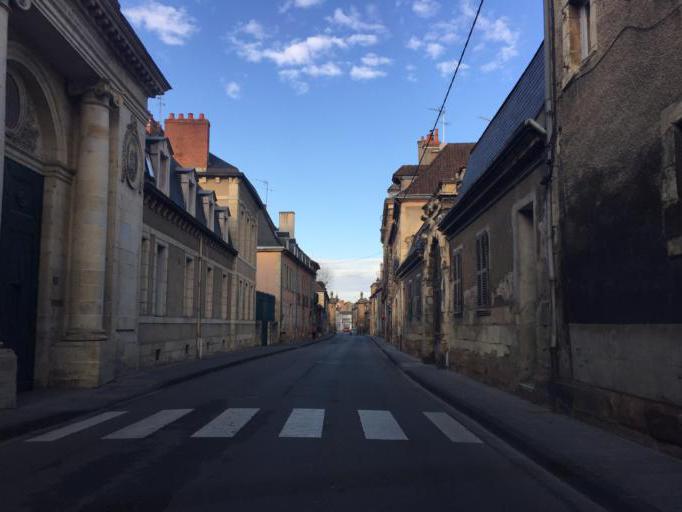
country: FR
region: Auvergne
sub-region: Departement de l'Allier
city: Moulins
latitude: 46.5692
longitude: 3.3299
